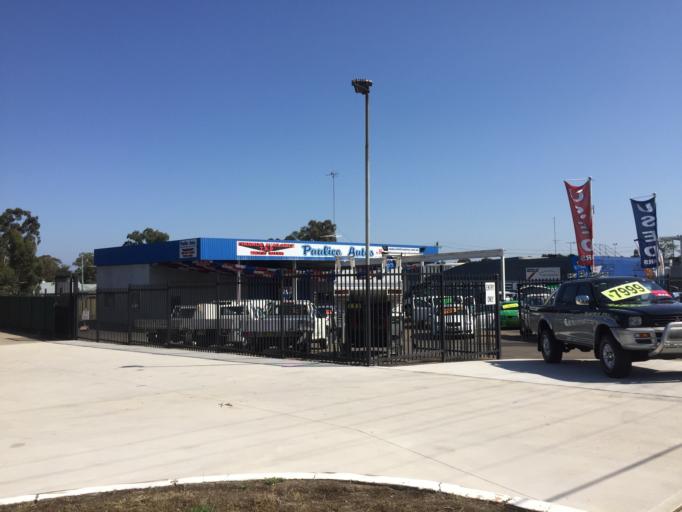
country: AU
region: New South Wales
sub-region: Blacktown
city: Blacktown
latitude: -33.7588
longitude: 150.9141
